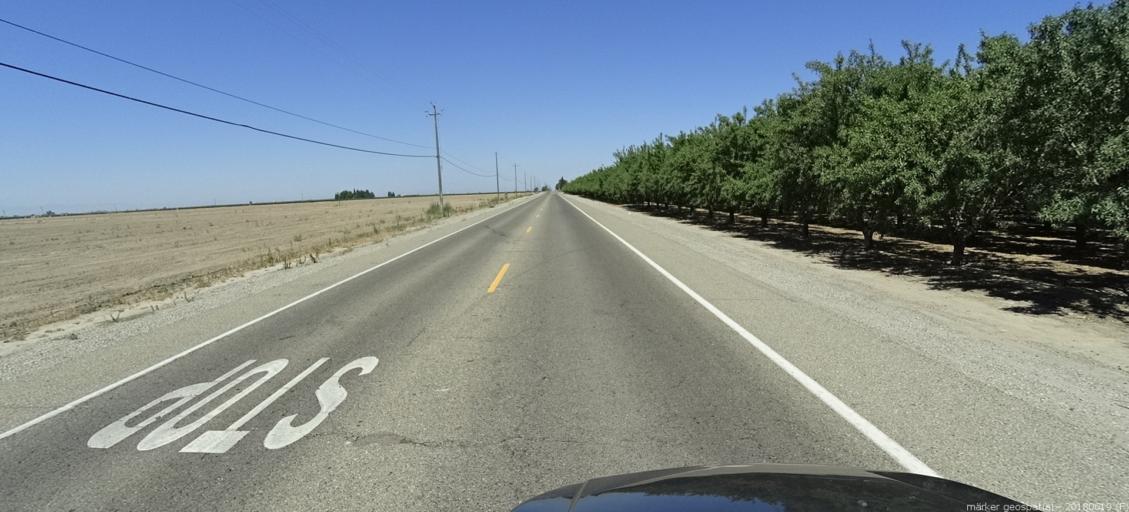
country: US
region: California
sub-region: Fresno County
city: Biola
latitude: 36.8514
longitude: -120.0587
